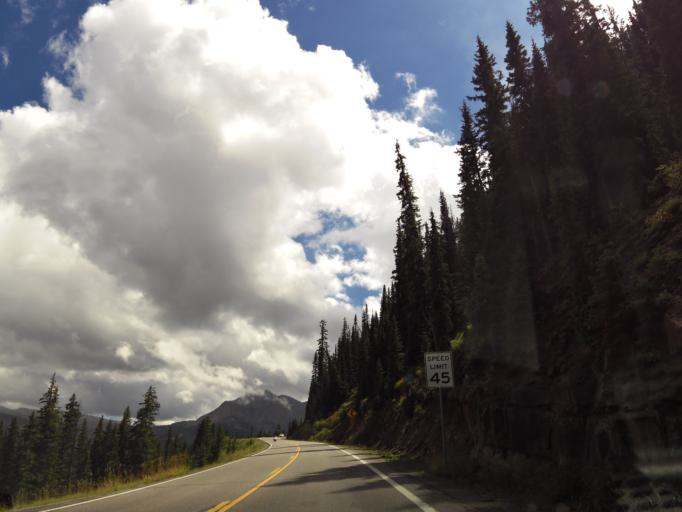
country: US
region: Colorado
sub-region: San Juan County
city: Silverton
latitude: 37.7075
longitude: -107.7711
